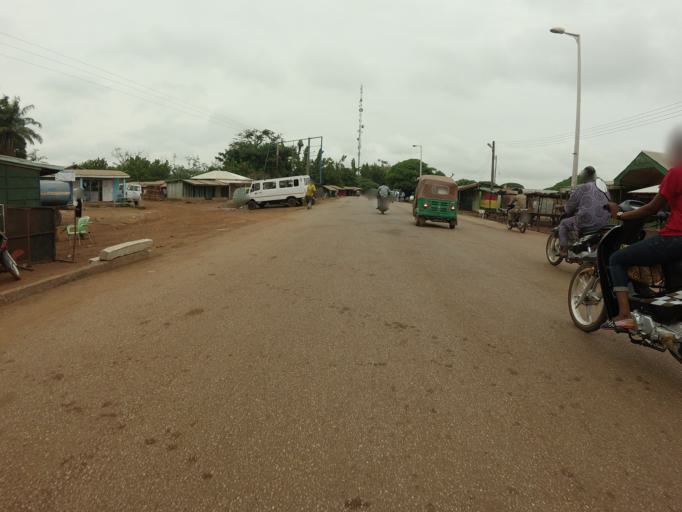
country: GH
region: Northern
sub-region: Yendi
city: Yendi
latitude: 9.4455
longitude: -0.0065
